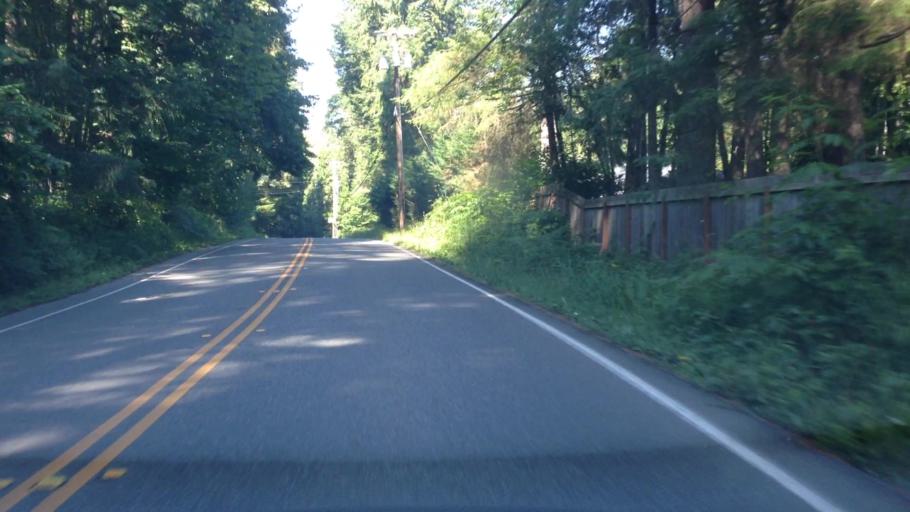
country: US
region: Washington
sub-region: King County
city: Lake Marcel-Stillwater
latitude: 47.7439
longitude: -121.9199
